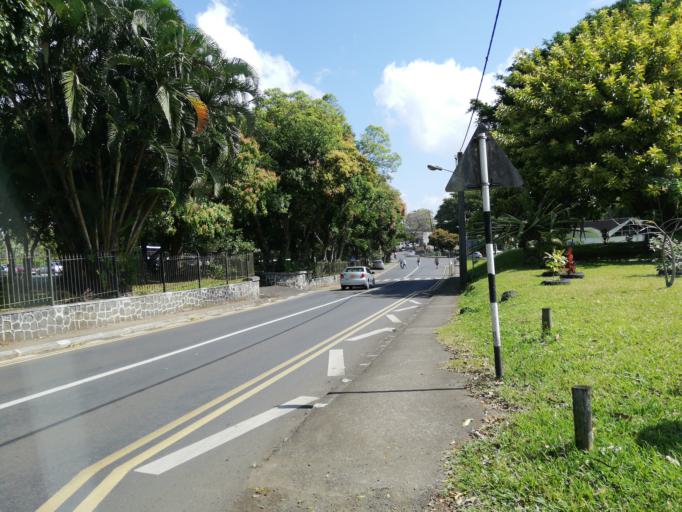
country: MU
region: Moka
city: Verdun
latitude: -20.2223
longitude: 57.5372
